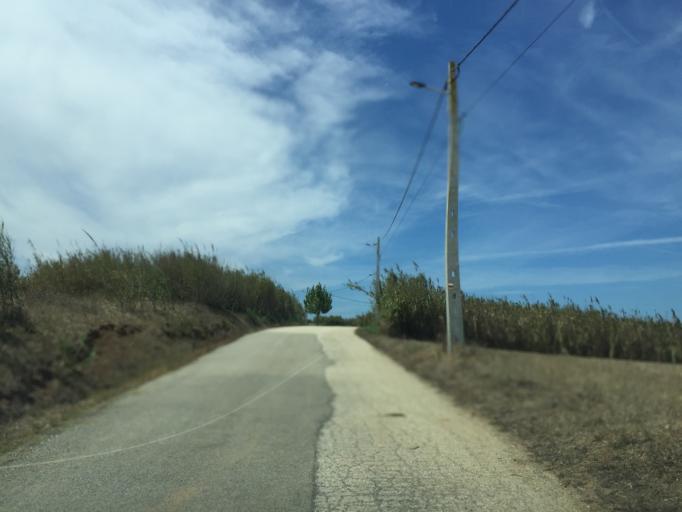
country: PT
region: Lisbon
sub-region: Lourinha
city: Lourinha
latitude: 39.2053
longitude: -9.3393
